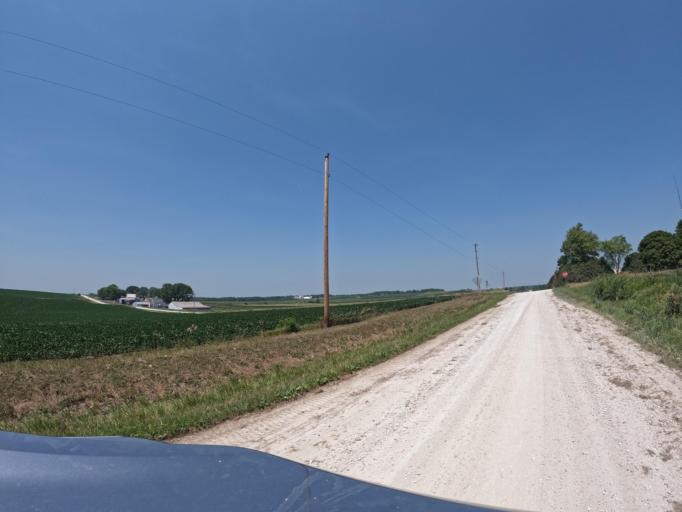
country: US
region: Iowa
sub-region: Keokuk County
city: Sigourney
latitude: 41.2861
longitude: -92.2096
